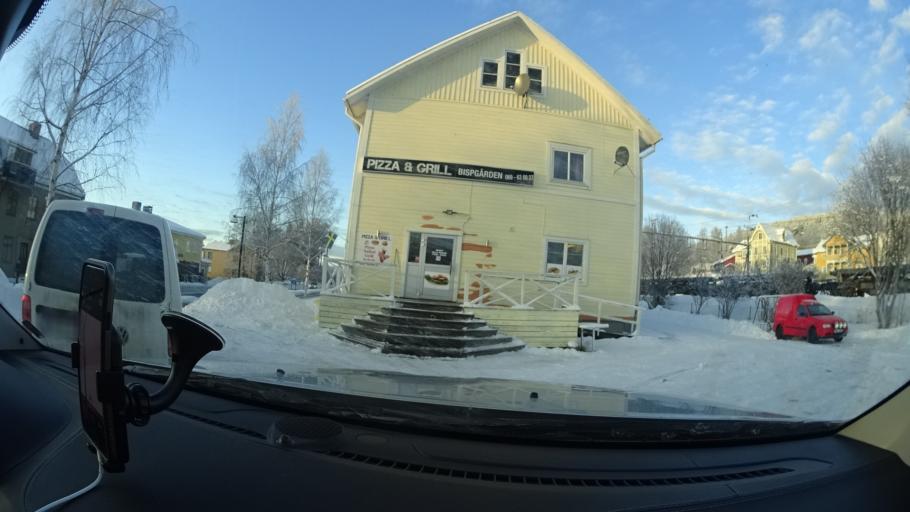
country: SE
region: Jaemtland
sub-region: Ragunda Kommun
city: Hammarstrand
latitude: 63.0286
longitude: 16.6200
